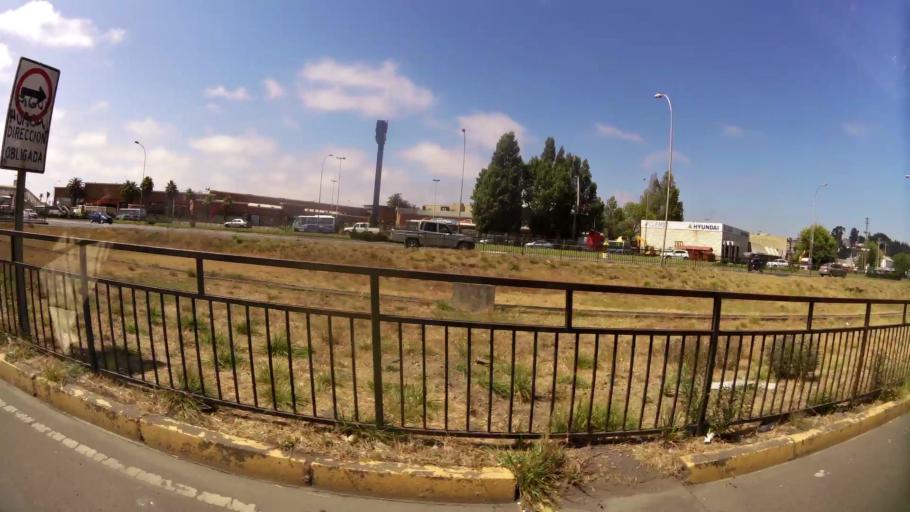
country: CL
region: Biobio
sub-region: Provincia de Concepcion
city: Concepcion
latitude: -36.7929
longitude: -73.0703
